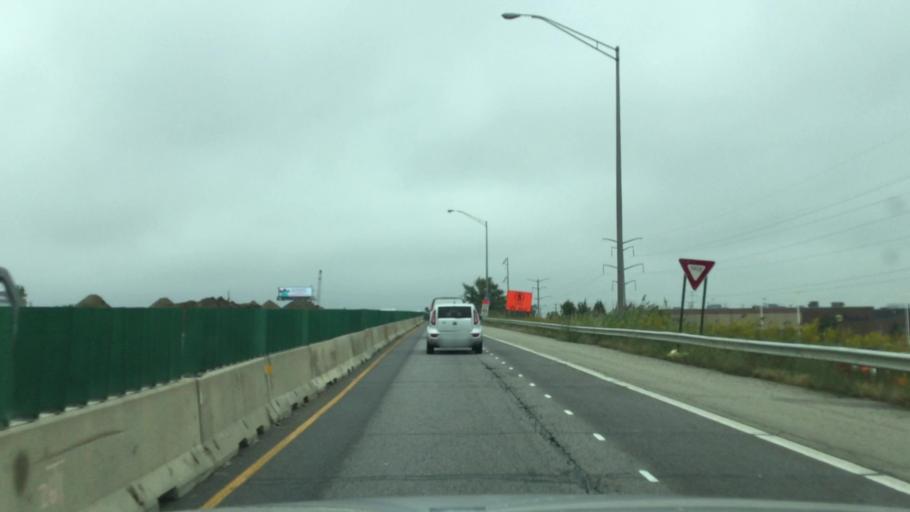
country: US
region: Illinois
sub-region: Cook County
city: Northbrook
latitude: 42.1468
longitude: -87.8352
